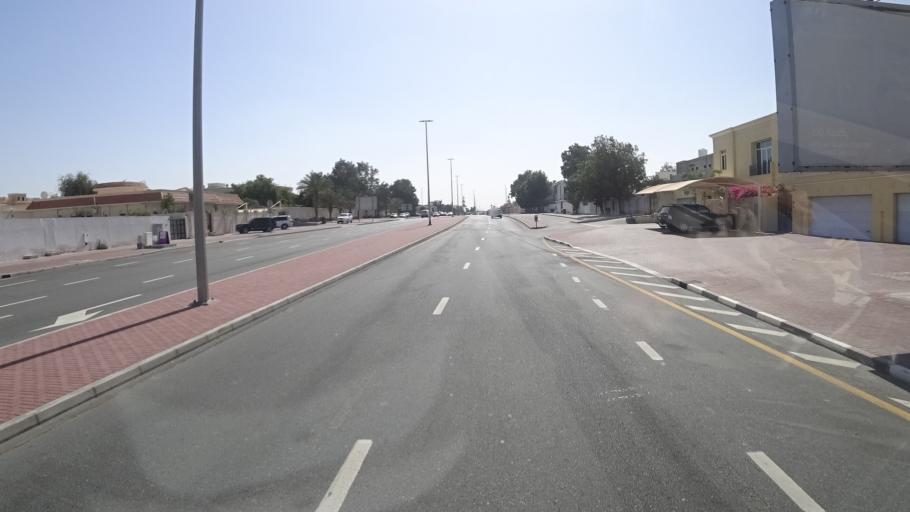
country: AE
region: Dubai
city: Dubai
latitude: 25.1596
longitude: 55.2085
